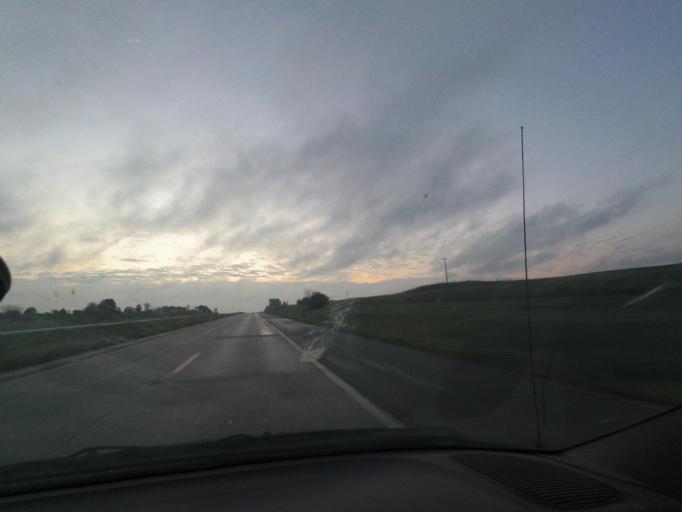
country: US
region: Missouri
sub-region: Linn County
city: Marceline
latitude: 39.7611
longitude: -92.9573
